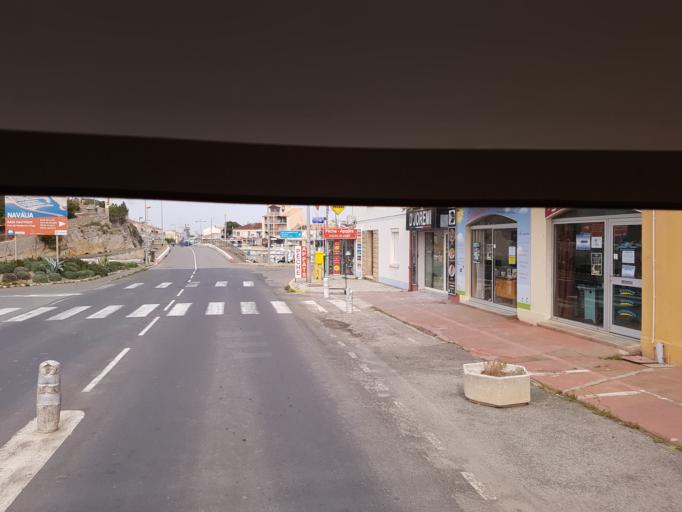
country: FR
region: Languedoc-Roussillon
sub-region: Departement de l'Aude
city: Fleury
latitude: 43.1701
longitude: 3.1798
